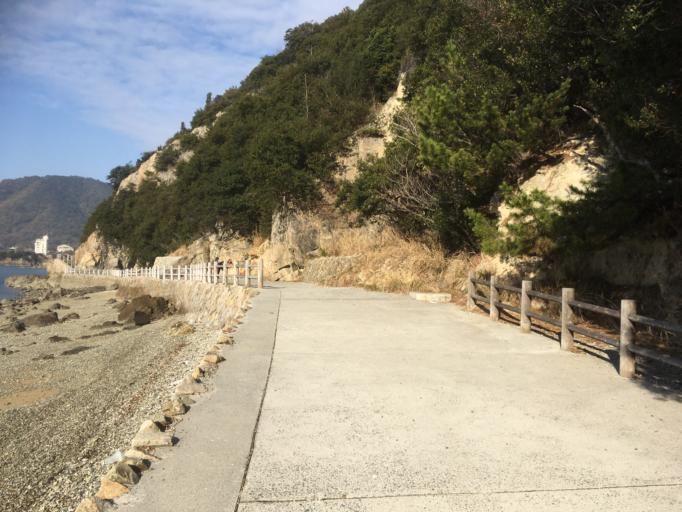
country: JP
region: Hiroshima
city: Fukuyama
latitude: 34.3821
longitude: 133.3938
